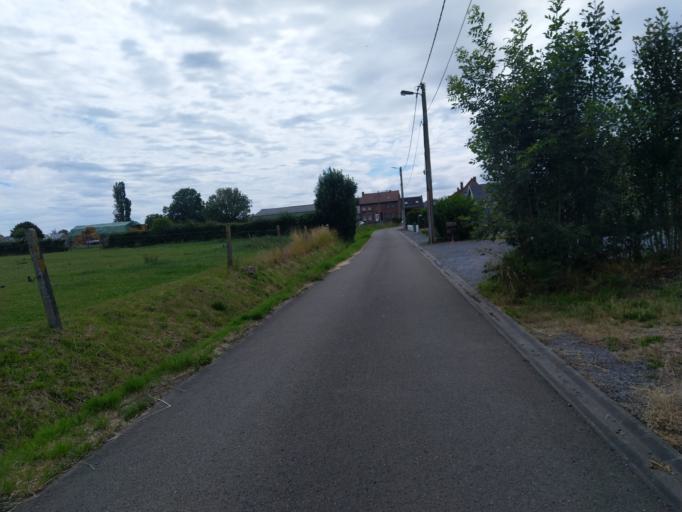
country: BE
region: Wallonia
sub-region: Province du Hainaut
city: Jurbise
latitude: 50.5218
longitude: 3.8559
